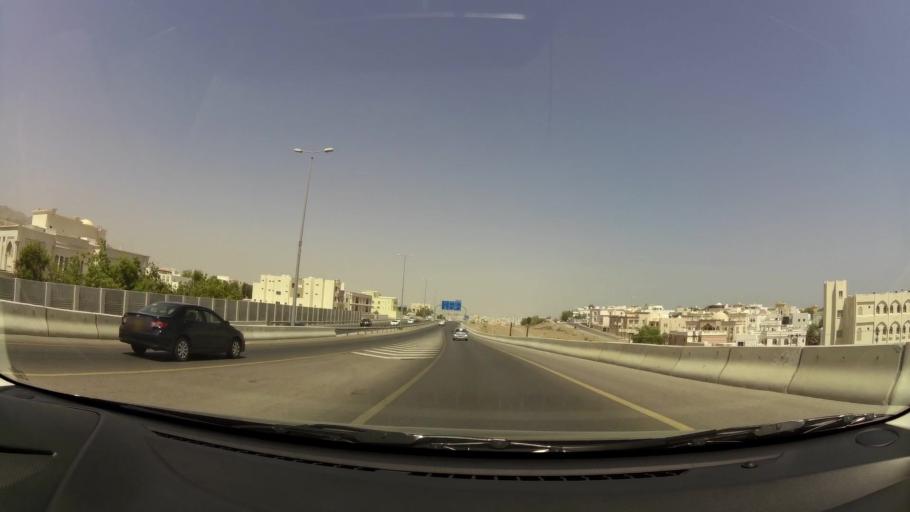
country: OM
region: Muhafazat Masqat
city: Bawshar
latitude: 23.5901
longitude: 58.4574
